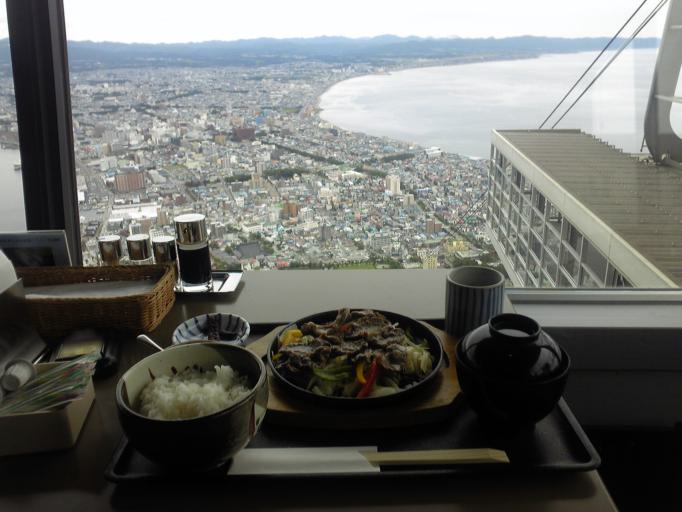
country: JP
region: Hokkaido
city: Hakodate
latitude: 41.7612
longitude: 140.7141
